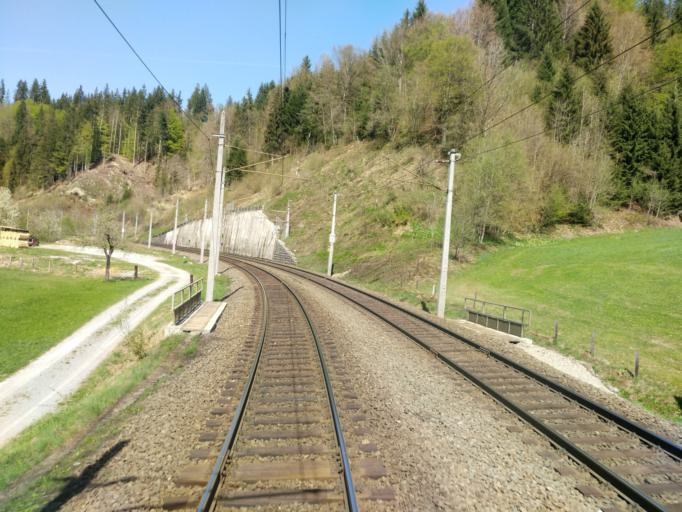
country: AT
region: Tyrol
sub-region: Politischer Bezirk Kitzbuhel
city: Westendorf
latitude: 47.4244
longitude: 12.1870
